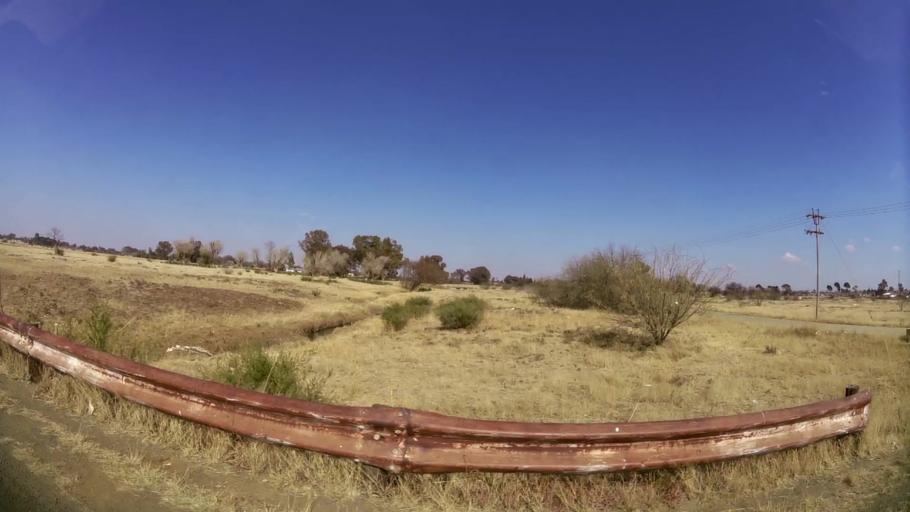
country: ZA
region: Orange Free State
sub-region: Mangaung Metropolitan Municipality
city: Bloemfontein
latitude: -29.1558
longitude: 26.3089
